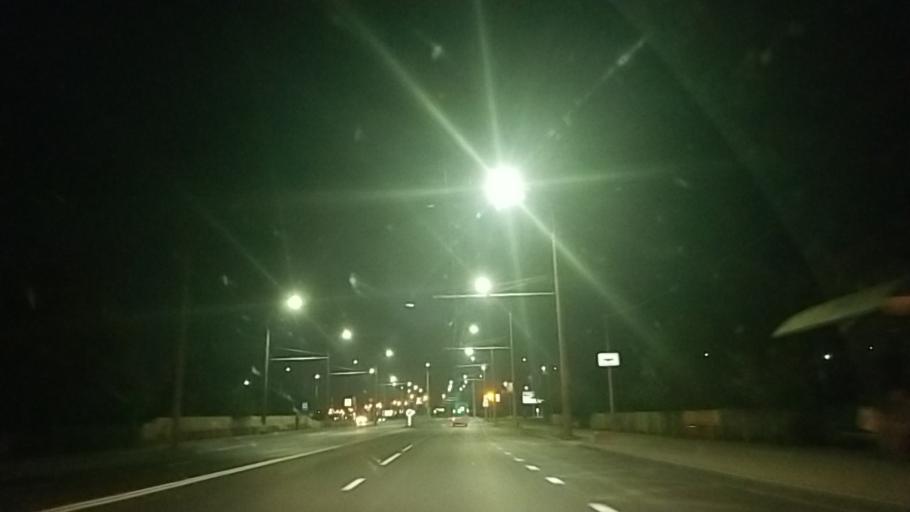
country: BY
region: Brest
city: Brest
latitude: 52.0758
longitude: 23.7672
